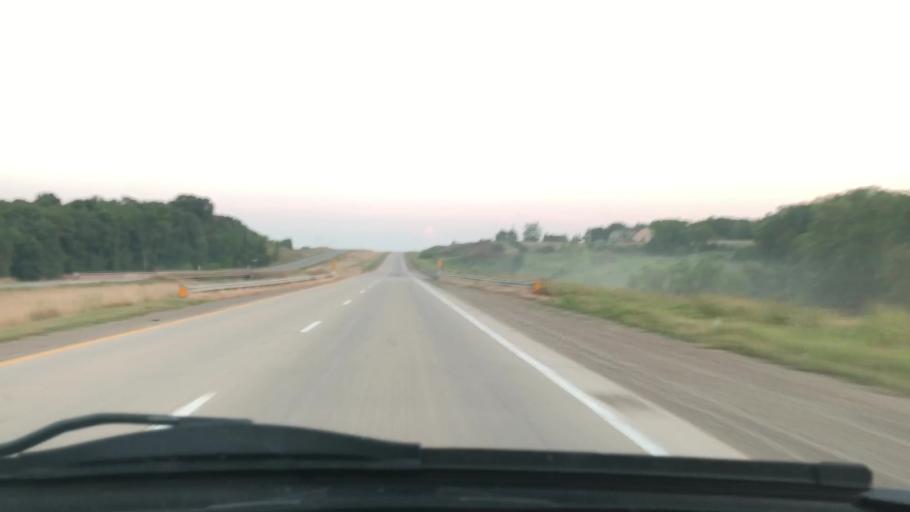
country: US
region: Iowa
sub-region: Henry County
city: Mount Pleasant
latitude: 40.8581
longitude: -91.5651
